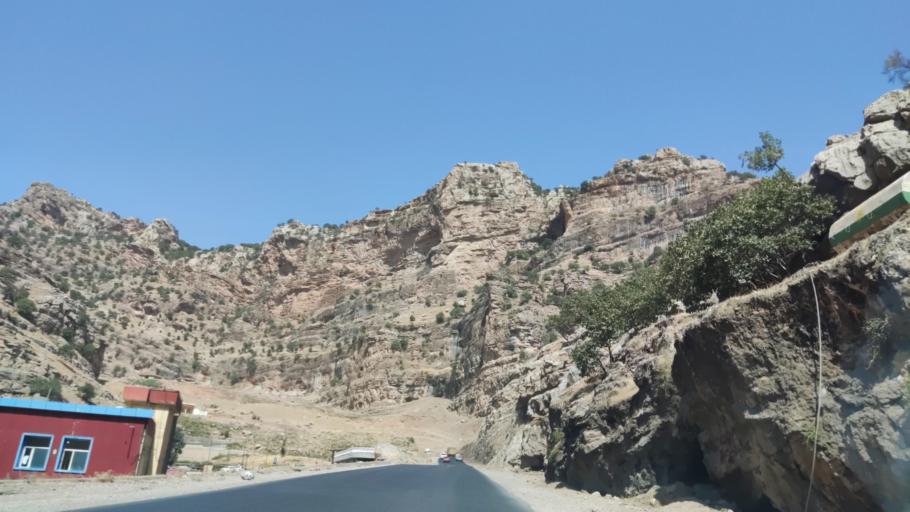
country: IQ
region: Arbil
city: Ruwandiz
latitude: 36.6310
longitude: 44.4481
